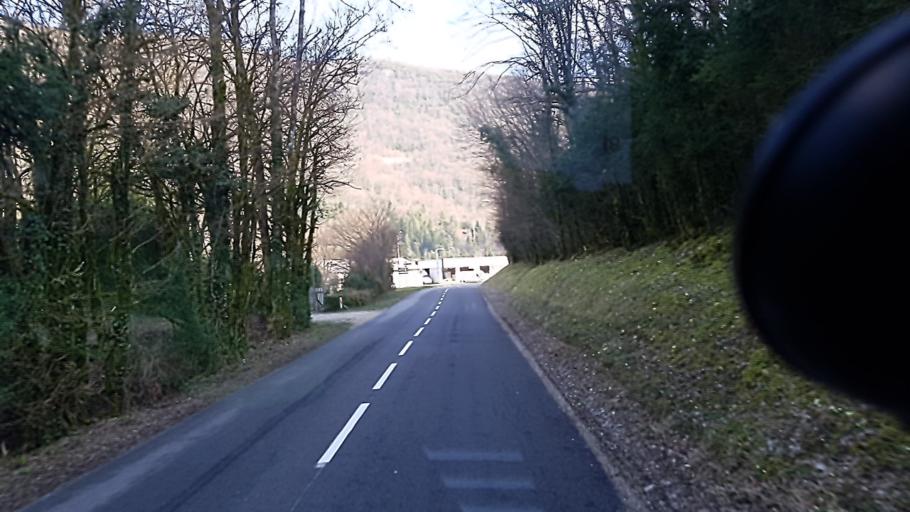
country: FR
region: Rhone-Alpes
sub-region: Departement de l'Ain
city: Dortan
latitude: 46.3401
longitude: 5.6454
